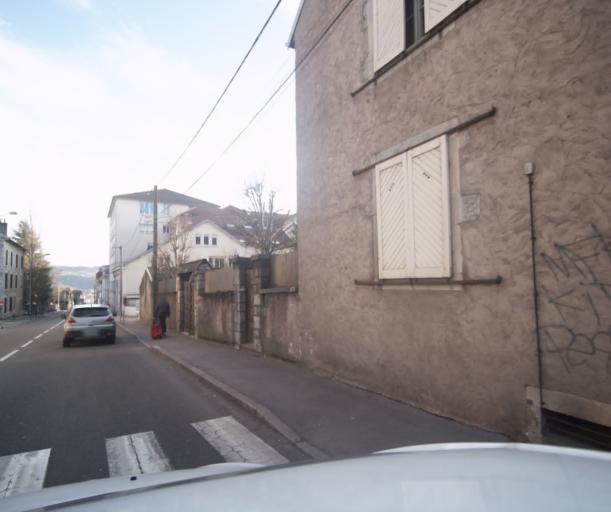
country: FR
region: Franche-Comte
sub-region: Departement du Doubs
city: Besancon
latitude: 47.2521
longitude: 6.0150
